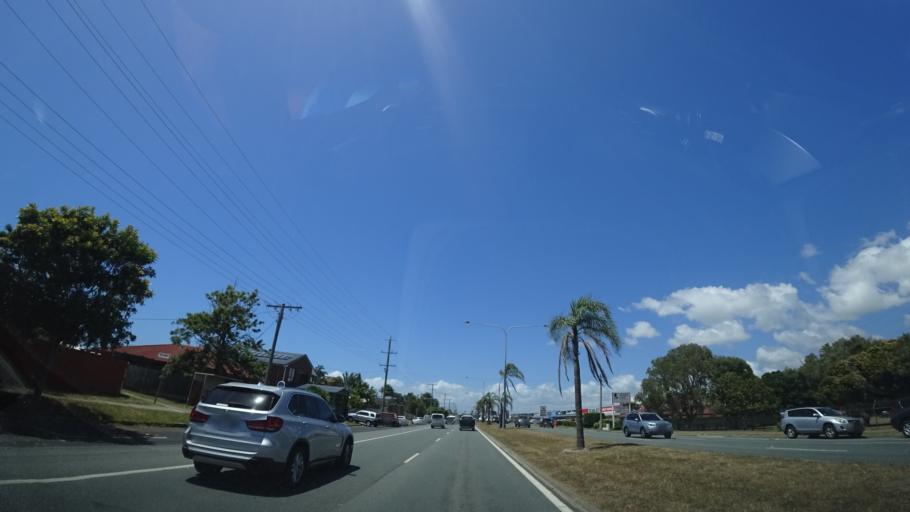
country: AU
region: Queensland
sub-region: Sunshine Coast
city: Mooloolaba
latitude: -26.7222
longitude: 153.1296
